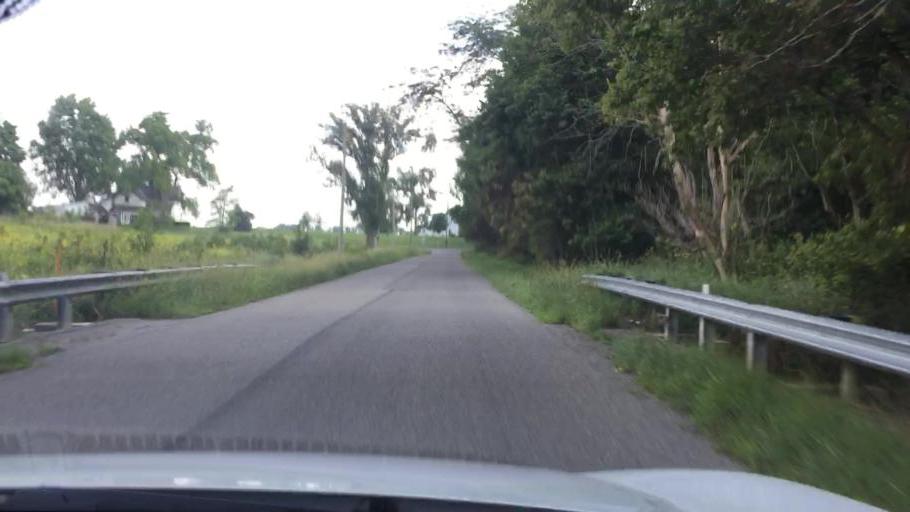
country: US
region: Ohio
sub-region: Champaign County
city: North Lewisburg
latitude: 40.2426
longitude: -83.5218
